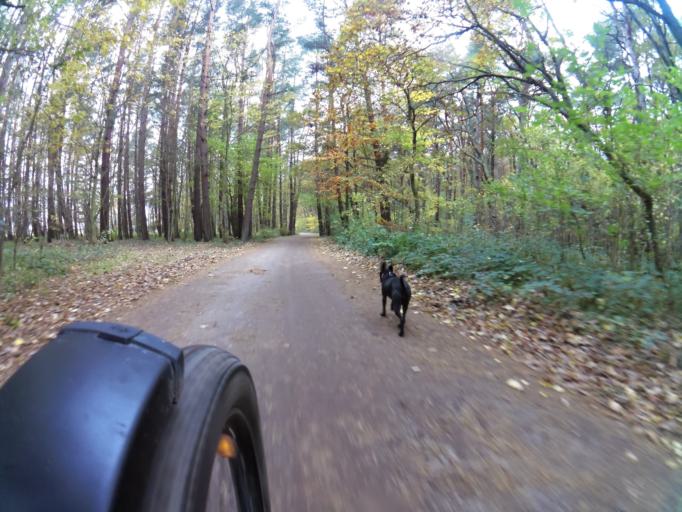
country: PL
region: Pomeranian Voivodeship
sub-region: Powiat pucki
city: Krokowa
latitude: 54.8295
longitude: 18.1398
